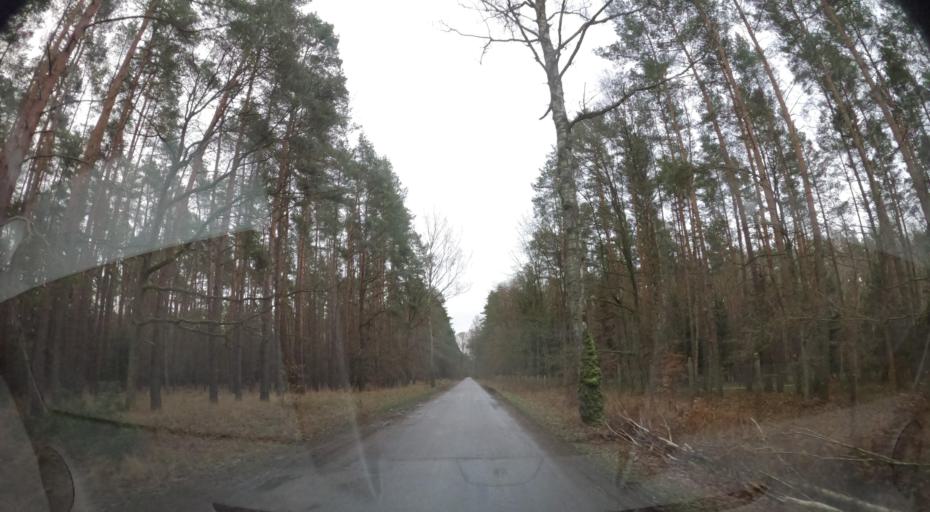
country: PL
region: Greater Poland Voivodeship
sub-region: Powiat zlotowski
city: Krajenka
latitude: 53.2868
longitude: 17.0642
